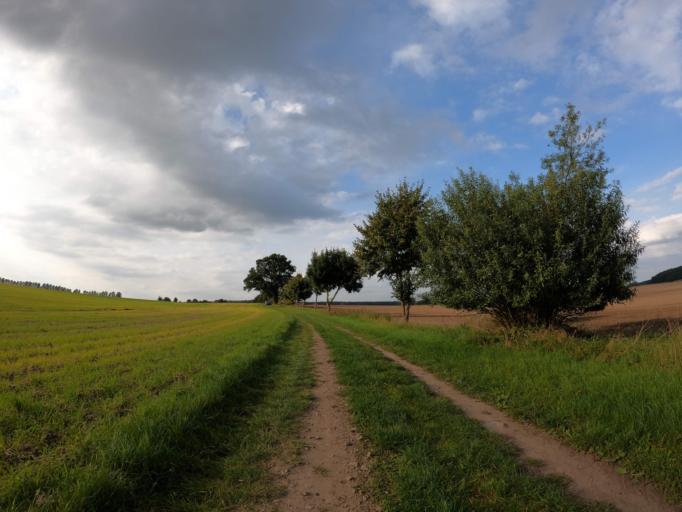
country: DE
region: Mecklenburg-Vorpommern
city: Klink
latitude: 53.4491
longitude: 12.5236
